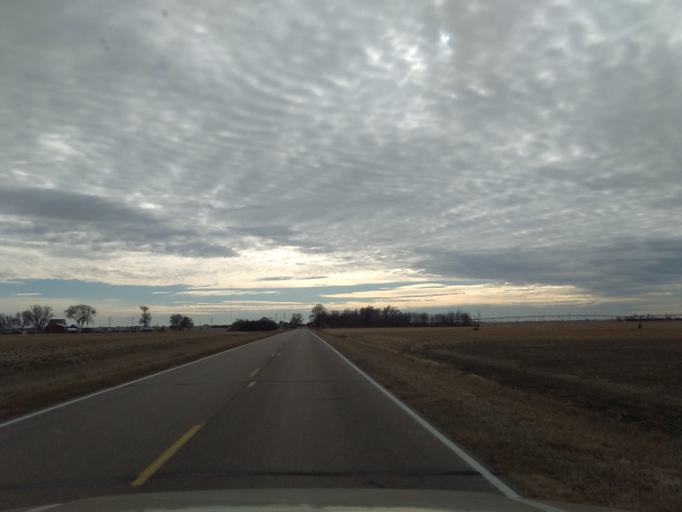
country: US
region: Nebraska
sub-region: Buffalo County
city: Gibbon
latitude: 40.6519
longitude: -98.8473
